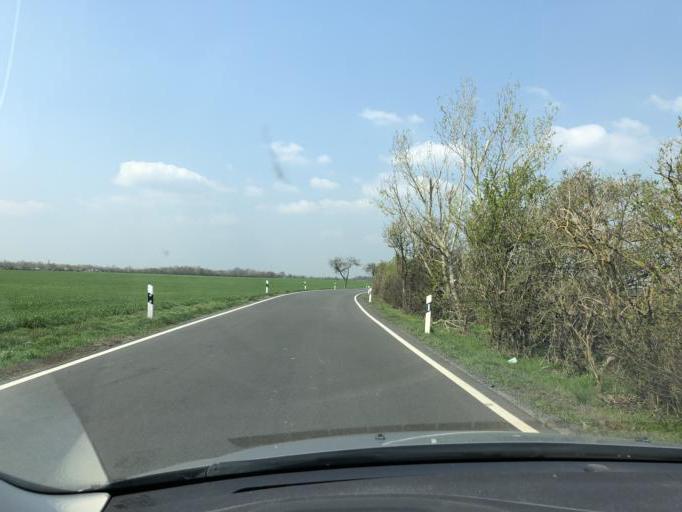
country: DE
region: Saxony
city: Wiedemar
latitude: 51.4888
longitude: 12.2173
